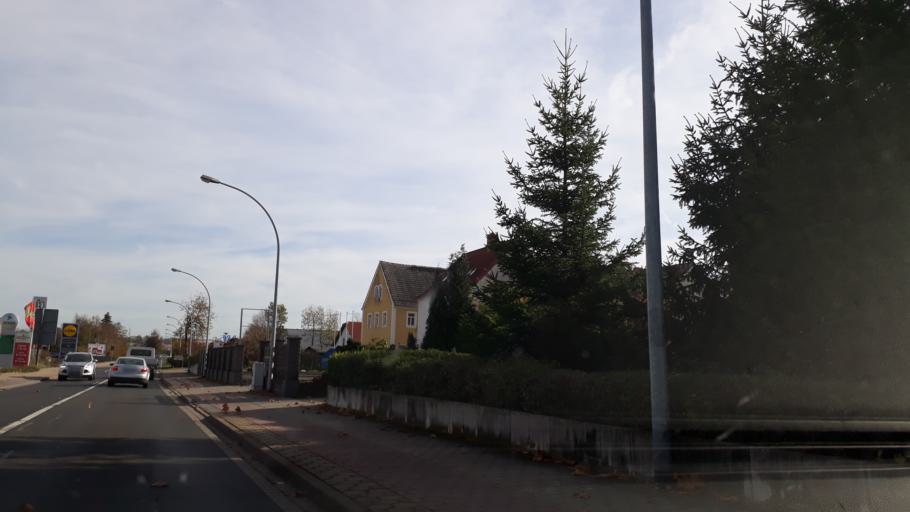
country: DE
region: Saxony
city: Dobeln
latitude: 51.1211
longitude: 13.1429
